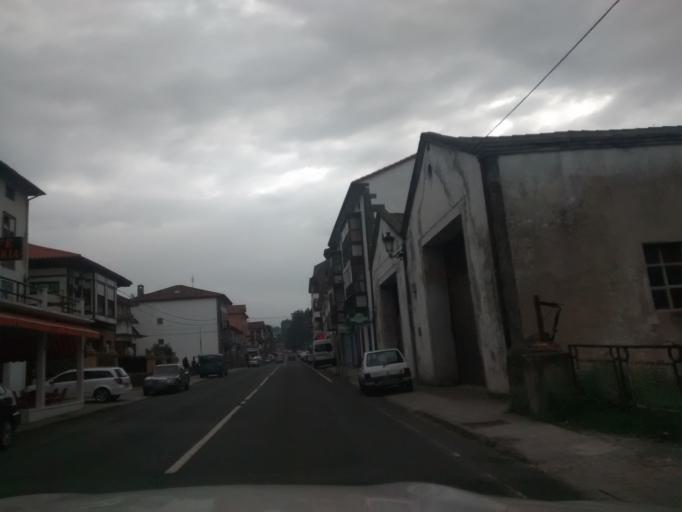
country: ES
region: Cantabria
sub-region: Provincia de Cantabria
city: Santiurde de Toranzo
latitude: 43.1970
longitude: -3.9229
